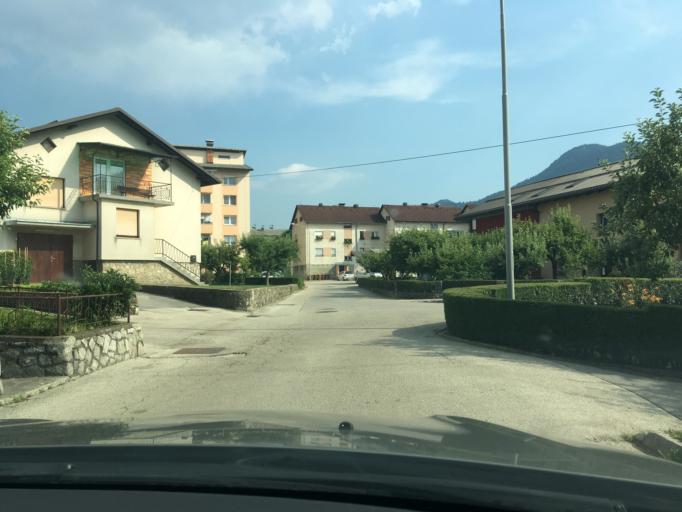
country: SI
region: Kocevje
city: Kocevje
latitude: 45.6450
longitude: 14.8557
